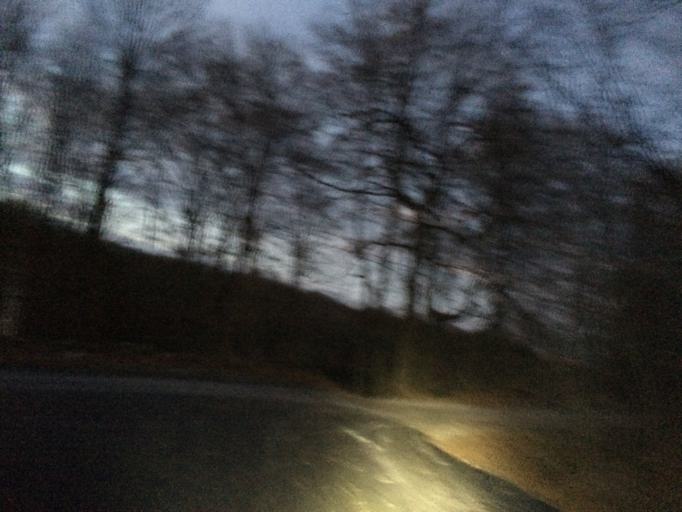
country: FR
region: Picardie
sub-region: Departement de l'Oise
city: Coye-la-Foret
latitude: 49.1546
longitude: 2.4797
